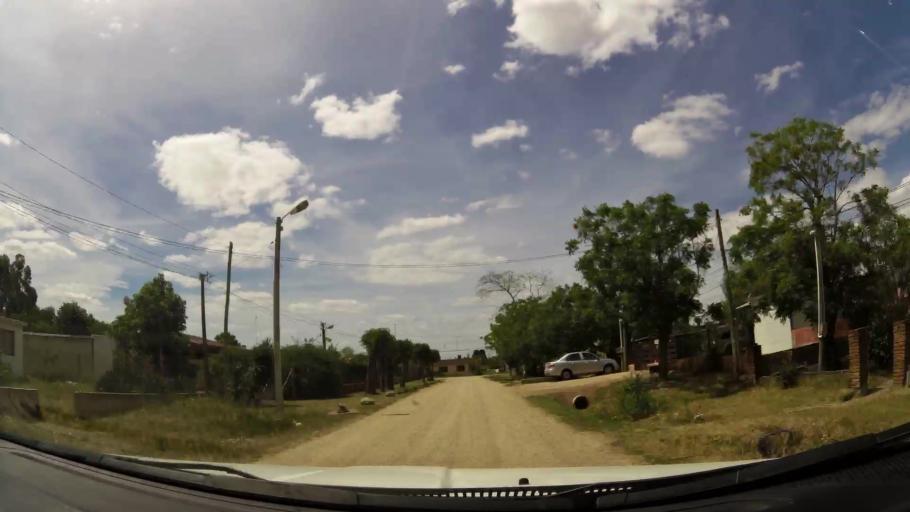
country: UY
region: San Jose
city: Delta del Tigre
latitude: -34.7497
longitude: -56.4570
